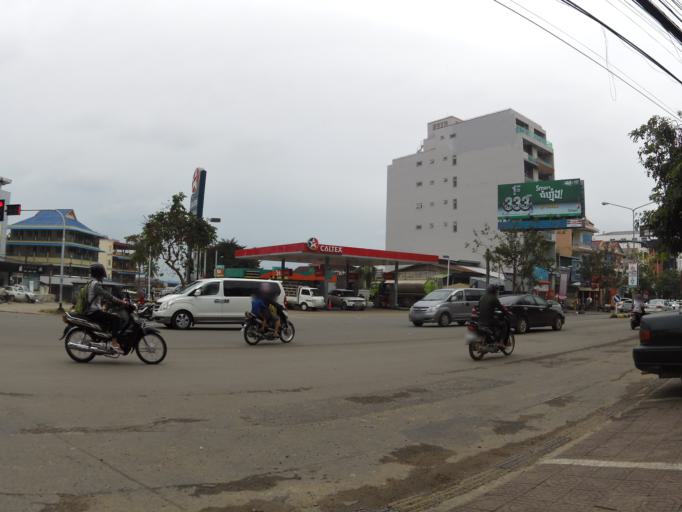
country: KH
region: Preah Sihanouk
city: Sihanoukville
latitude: 10.6235
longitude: 103.5249
